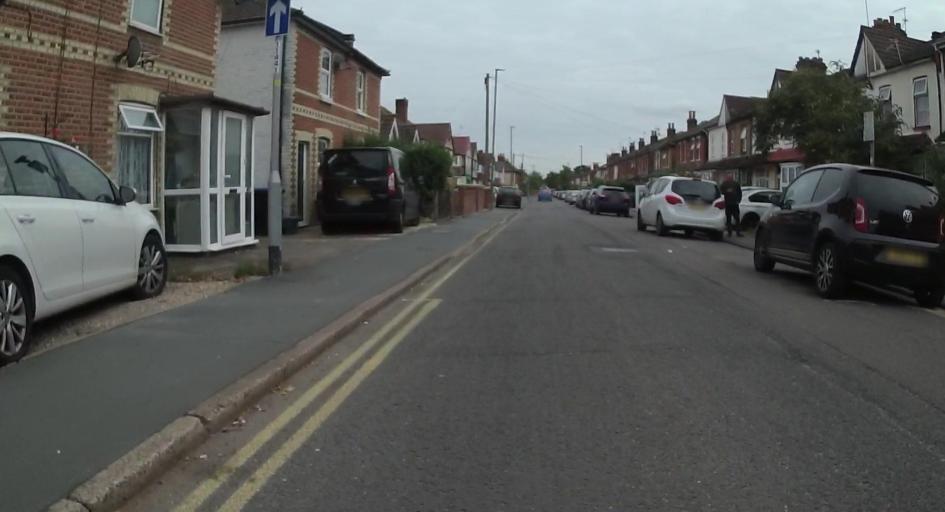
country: GB
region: England
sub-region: Surrey
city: Woking
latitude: 51.3235
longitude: -0.5489
